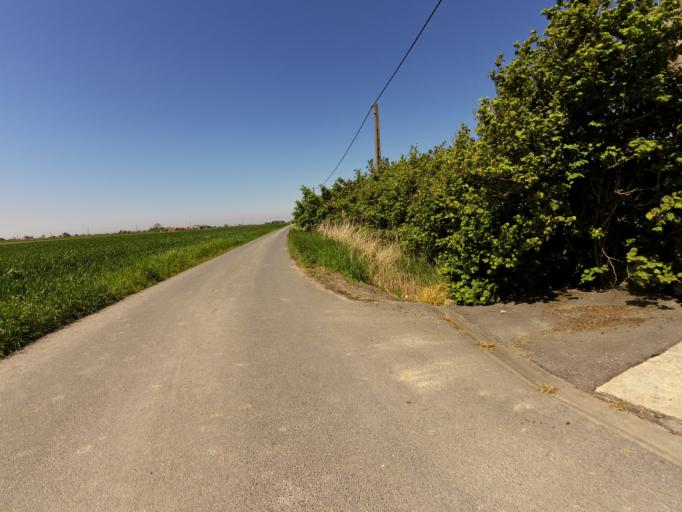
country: BE
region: Flanders
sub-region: Provincie West-Vlaanderen
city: Diksmuide
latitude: 51.0419
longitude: 2.8564
